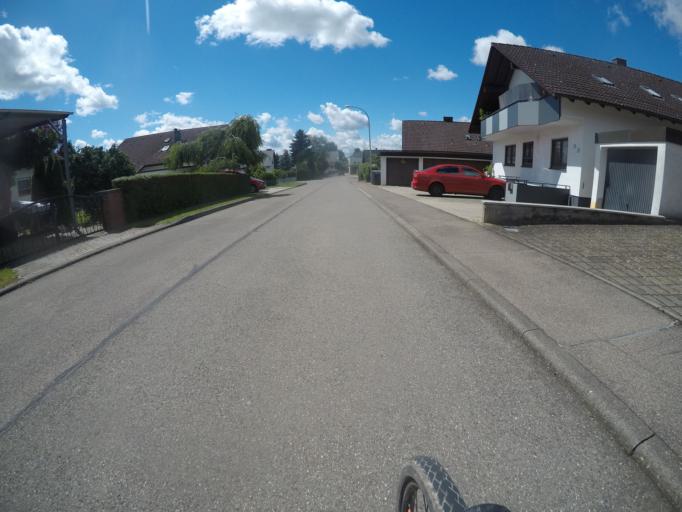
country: DE
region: Baden-Wuerttemberg
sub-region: Regierungsbezirk Stuttgart
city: Motzingen
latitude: 48.4930
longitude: 8.7504
